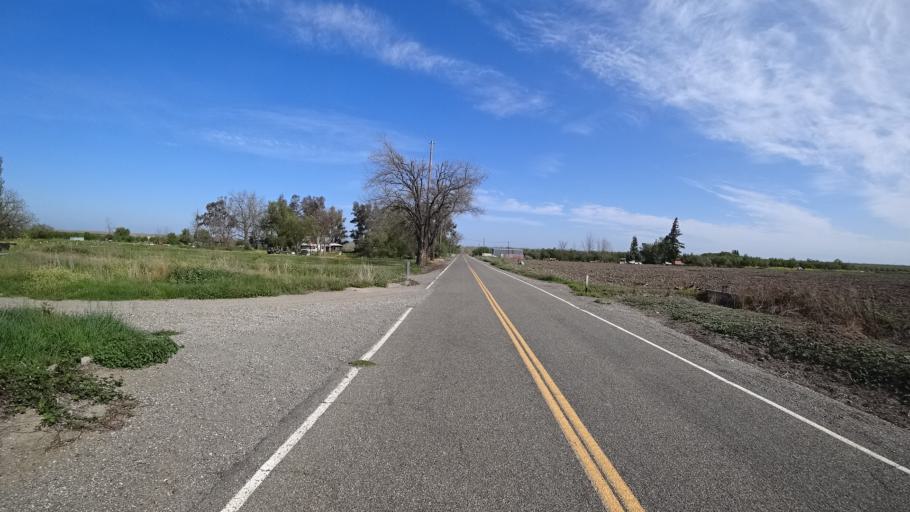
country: US
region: California
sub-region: Glenn County
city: Hamilton City
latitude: 39.6272
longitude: -122.0369
